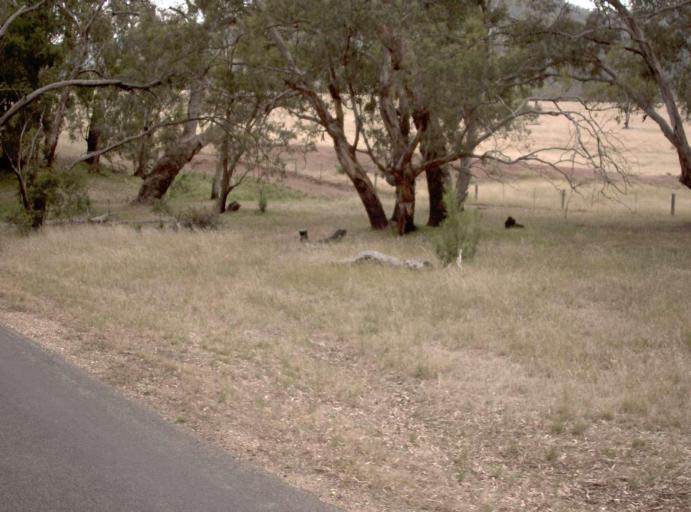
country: AU
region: Victoria
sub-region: Wellington
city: Heyfield
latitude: -37.6541
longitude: 146.6424
